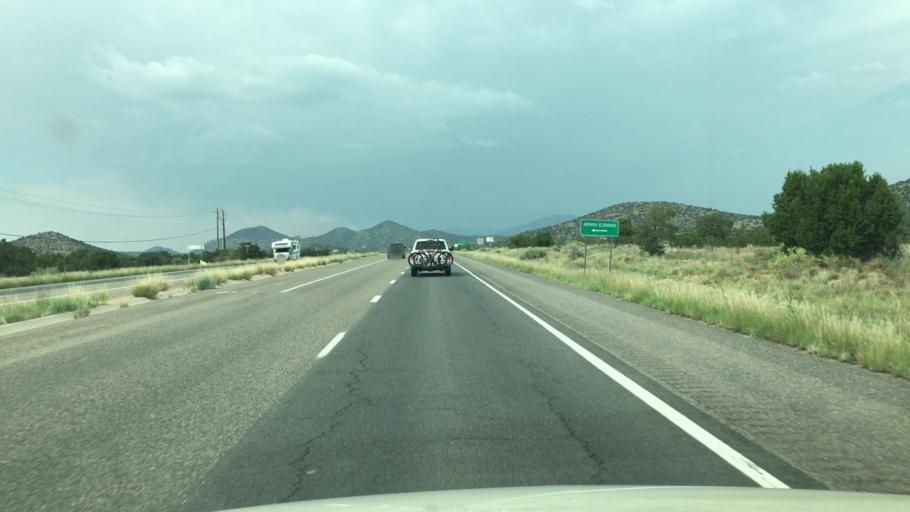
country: US
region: New Mexico
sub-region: Santa Fe County
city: Eldorado at Santa Fe
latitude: 35.5281
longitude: -105.8900
